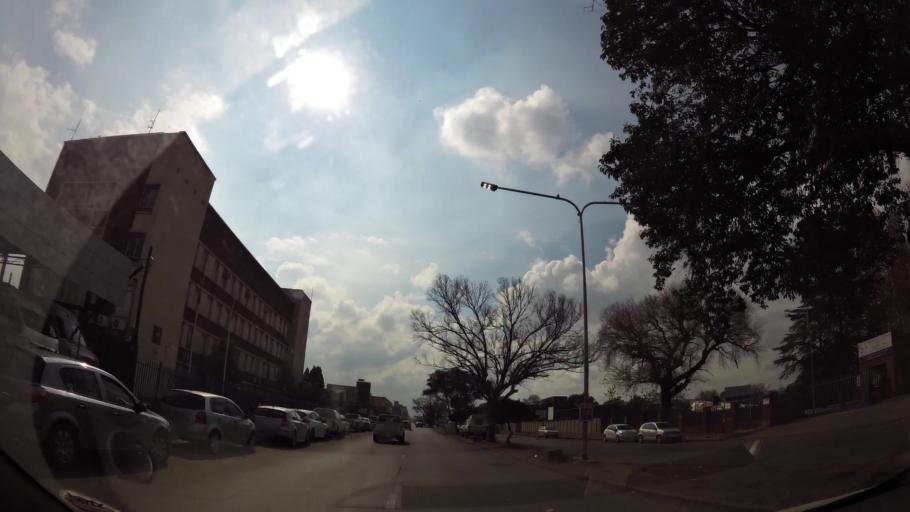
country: ZA
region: Gauteng
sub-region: Sedibeng District Municipality
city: Vereeniging
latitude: -26.6797
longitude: 27.9305
